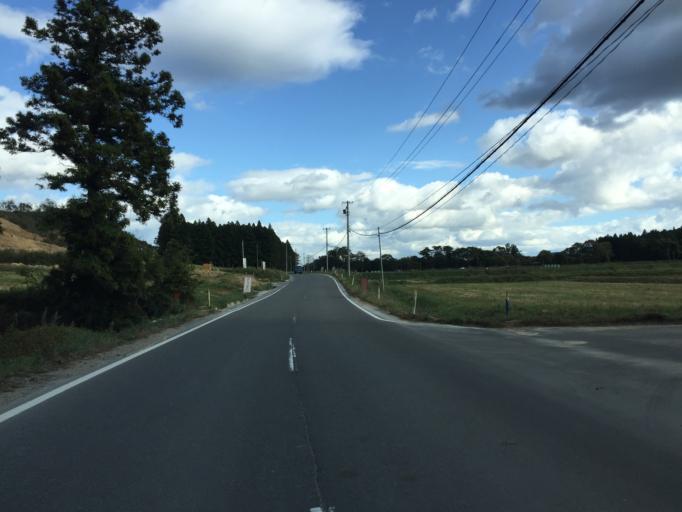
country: JP
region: Miyagi
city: Marumori
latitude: 37.8351
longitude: 140.8170
